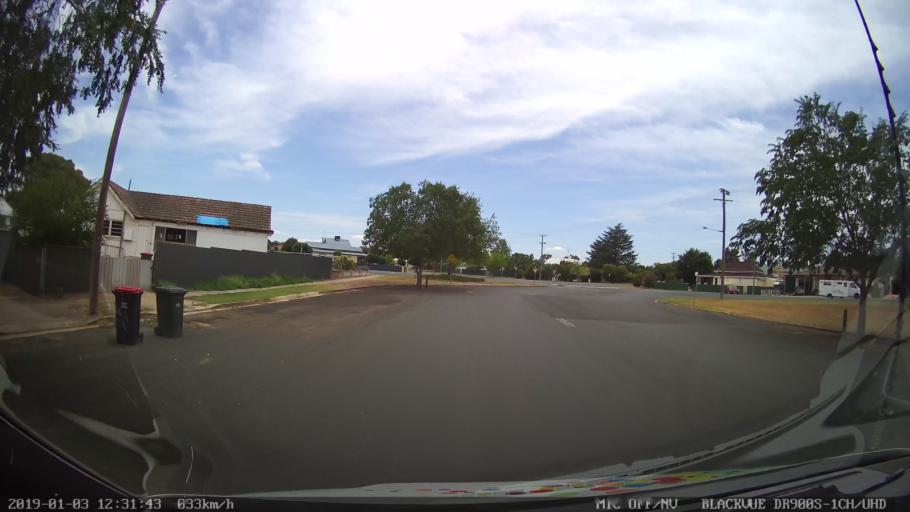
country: AU
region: New South Wales
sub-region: Weddin
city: Grenfell
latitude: -33.8937
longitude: 148.1644
